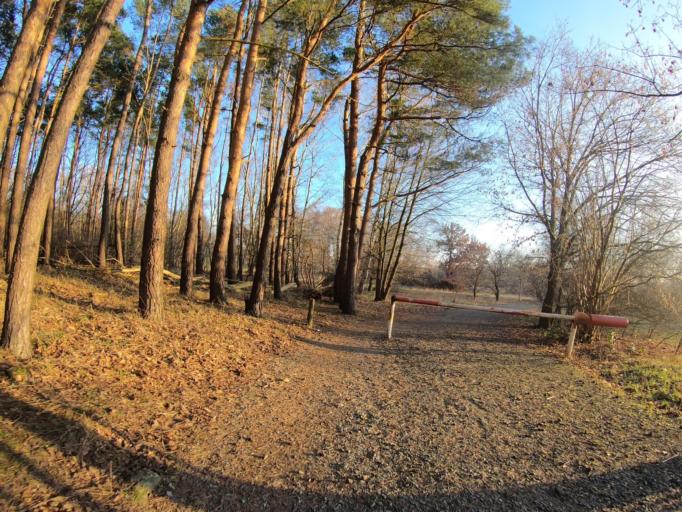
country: DE
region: Lower Saxony
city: Gifhorn
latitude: 52.4890
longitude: 10.5580
